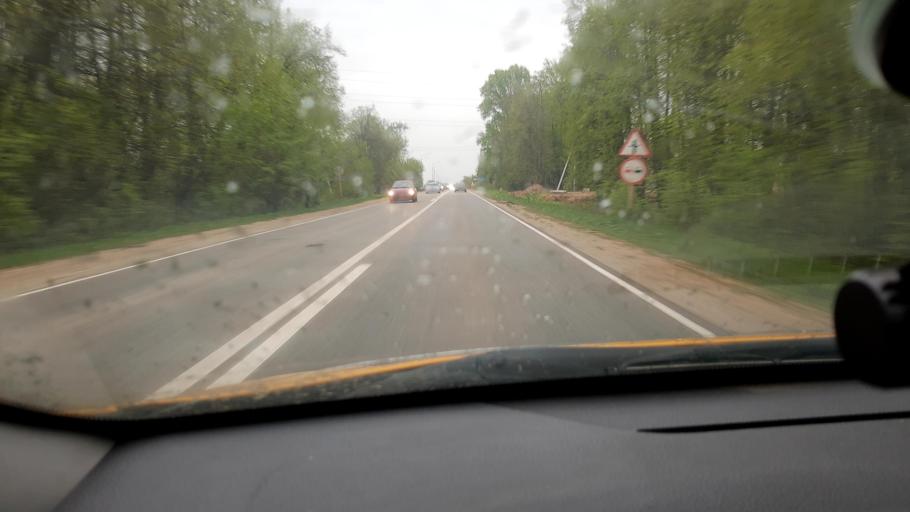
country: RU
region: Tula
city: Zaokskiy
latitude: 54.7672
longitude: 37.4364
